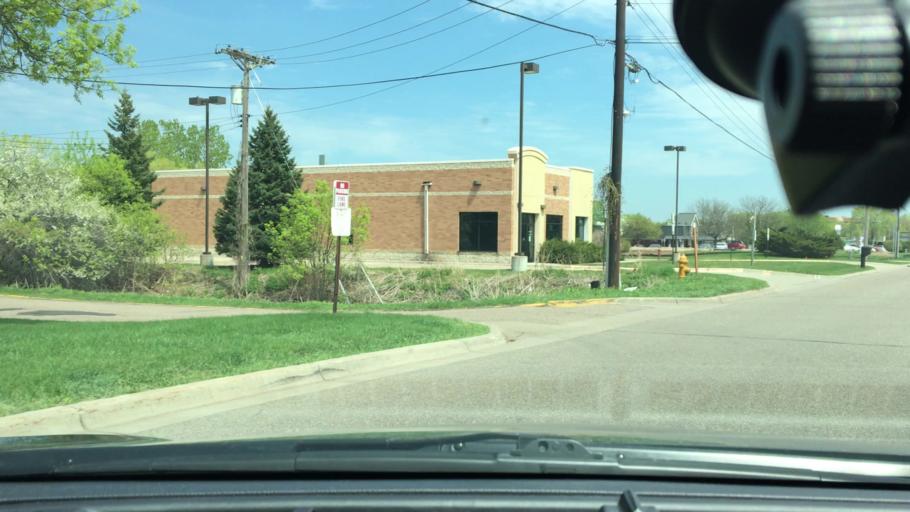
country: US
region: Minnesota
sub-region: Hennepin County
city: Golden Valley
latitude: 44.9847
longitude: -93.3957
